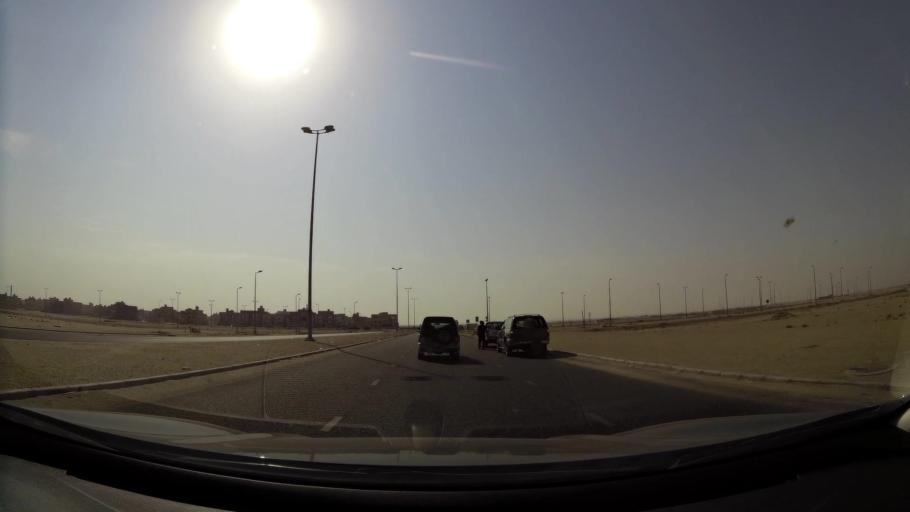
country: KW
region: Al Ahmadi
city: Al Wafrah
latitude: 28.7780
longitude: 48.0511
